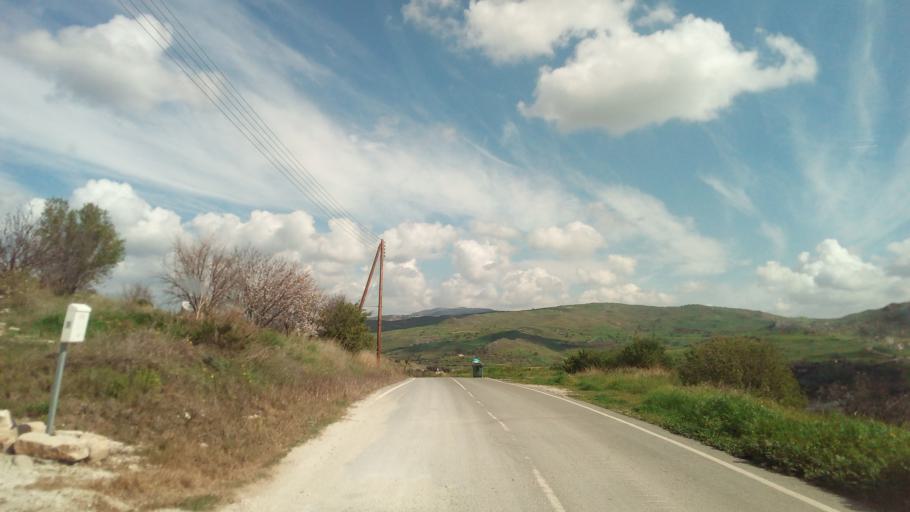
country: CY
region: Pafos
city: Mesogi
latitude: 34.7753
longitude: 32.5738
